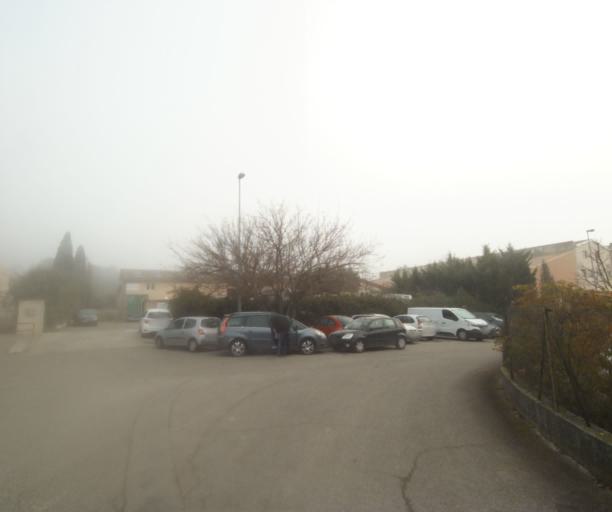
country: FR
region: Provence-Alpes-Cote d'Azur
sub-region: Departement des Bouches-du-Rhone
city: Eguilles
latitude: 43.5467
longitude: 5.3637
